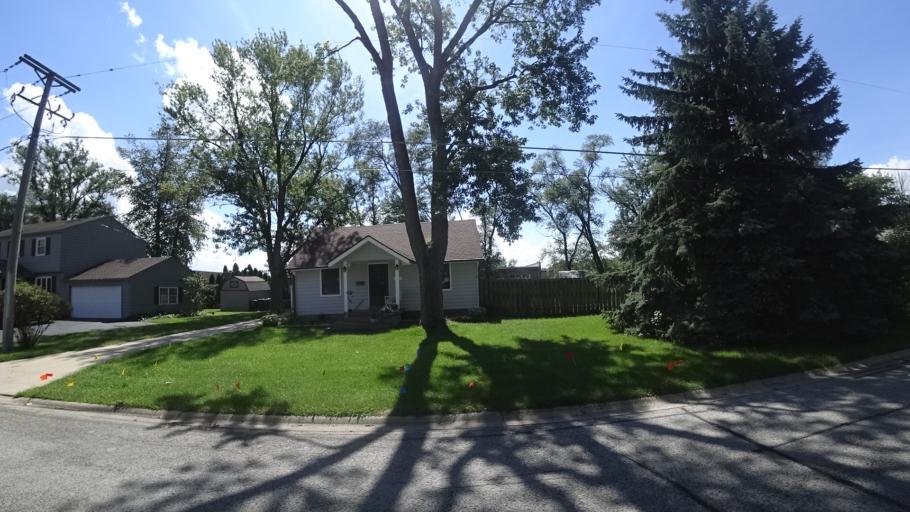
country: US
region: Illinois
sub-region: Cook County
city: Tinley Park
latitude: 41.5695
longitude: -87.7858
